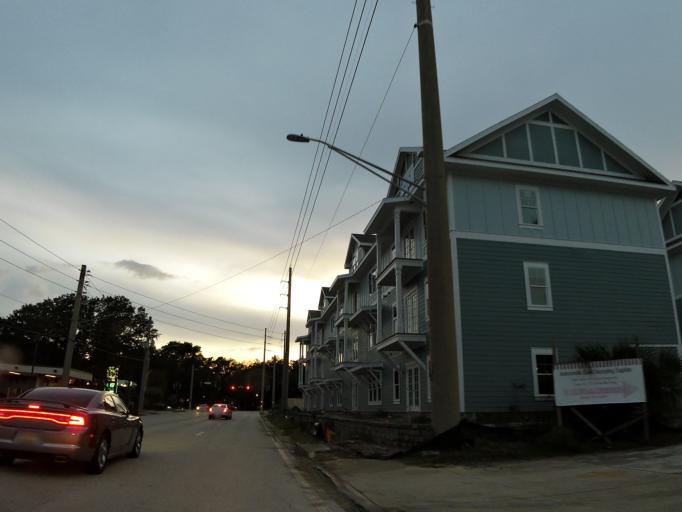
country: US
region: Florida
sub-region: Duval County
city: Jacksonville
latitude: 30.3645
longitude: -81.6057
